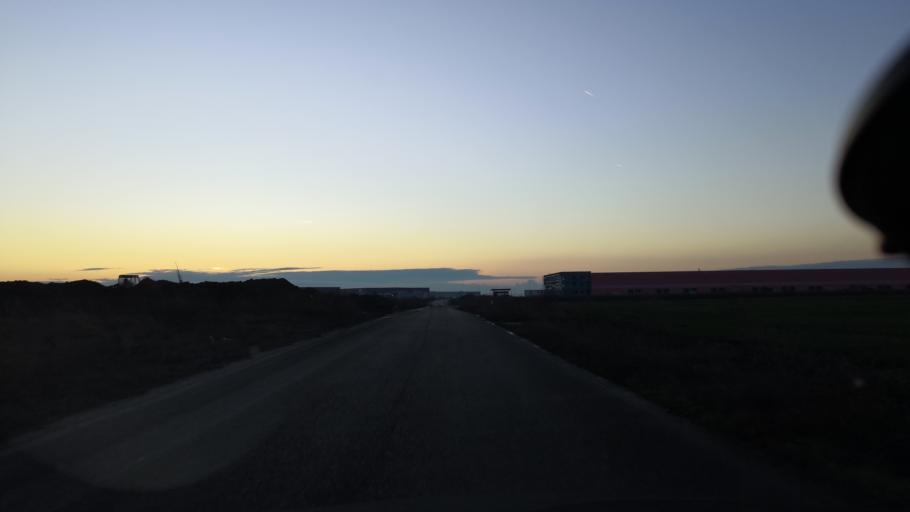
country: RS
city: Simanovci
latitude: 44.8900
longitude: 20.1039
